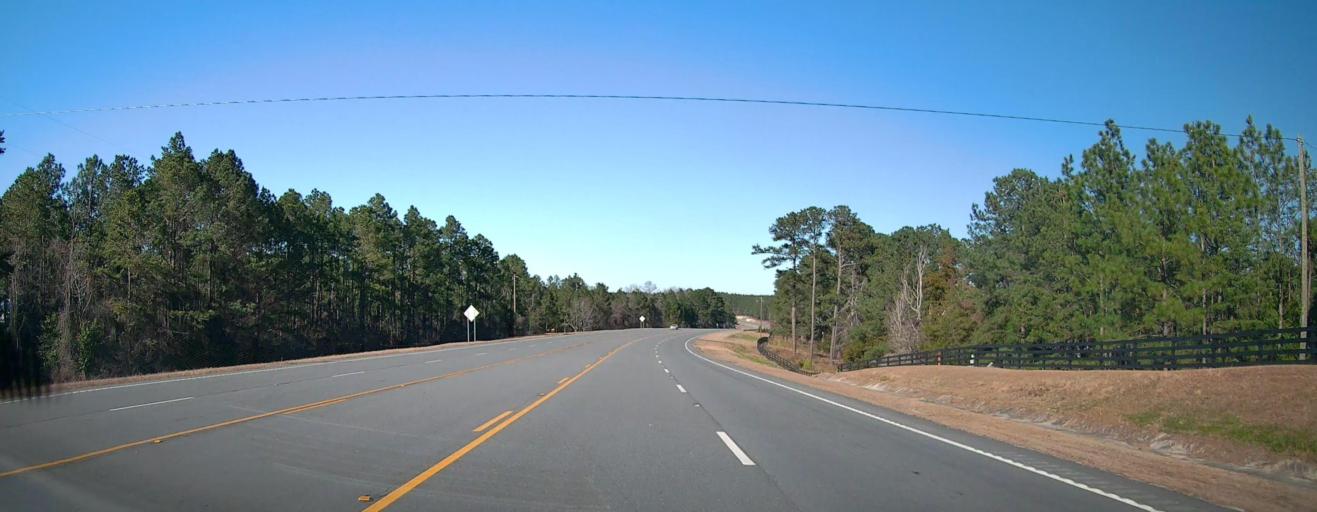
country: US
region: Georgia
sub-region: Taylor County
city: Butler
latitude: 32.5798
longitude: -84.2381
